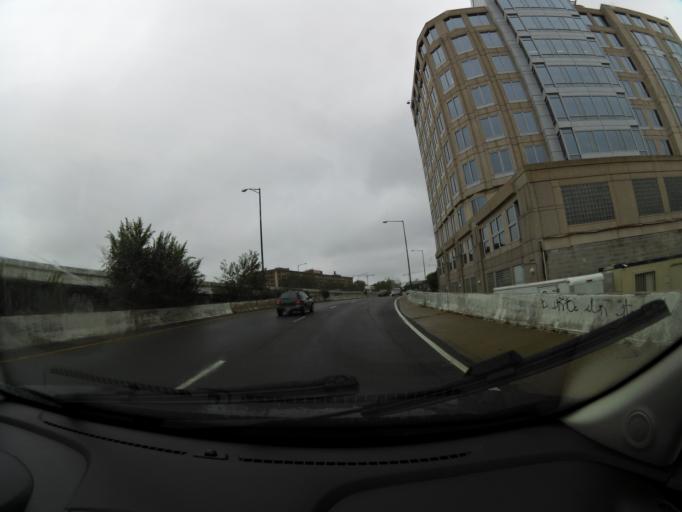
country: US
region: Washington, D.C.
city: Washington, D.C.
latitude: 38.8828
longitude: -77.0135
